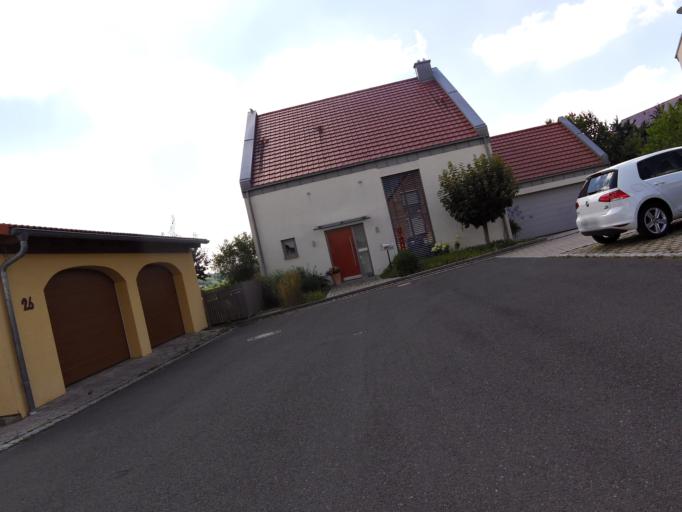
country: DE
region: Bavaria
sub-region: Regierungsbezirk Unterfranken
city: Gerbrunn
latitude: 49.7829
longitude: 9.9926
